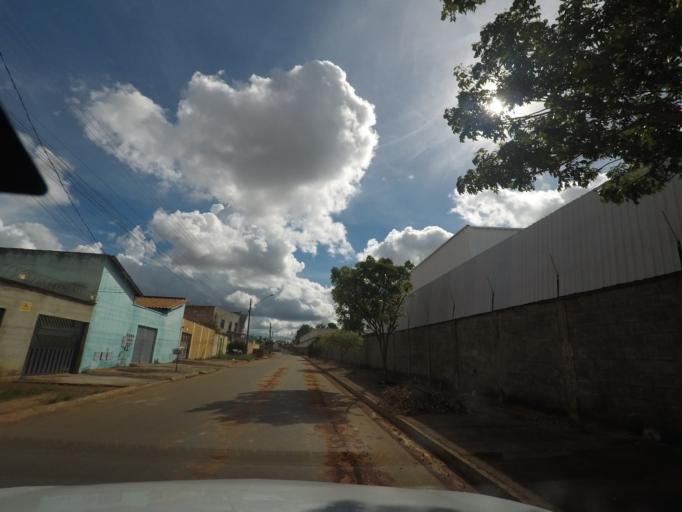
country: BR
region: Goias
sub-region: Goiania
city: Goiania
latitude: -16.7182
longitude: -49.3620
